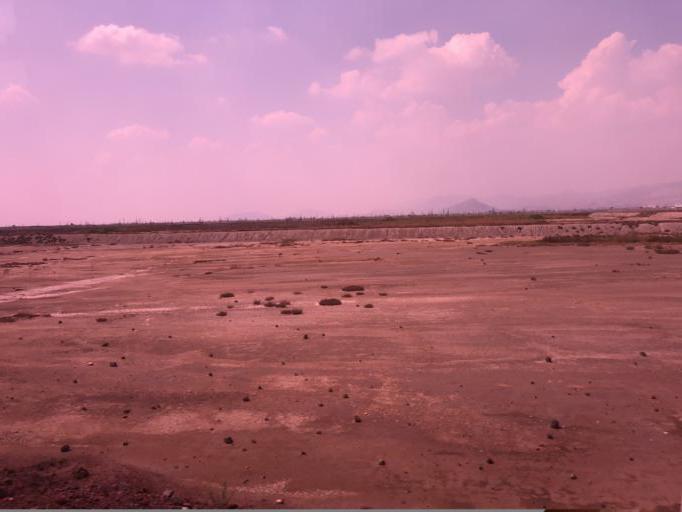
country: MX
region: Mexico
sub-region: Atenco
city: Colonia el Salado
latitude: 19.5482
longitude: -98.9848
